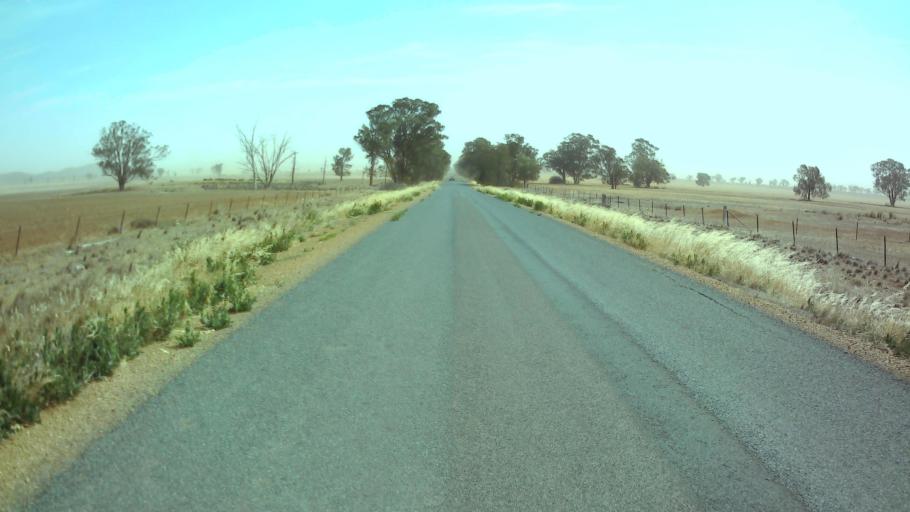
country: AU
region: New South Wales
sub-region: Weddin
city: Grenfell
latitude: -33.7633
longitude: 147.9883
